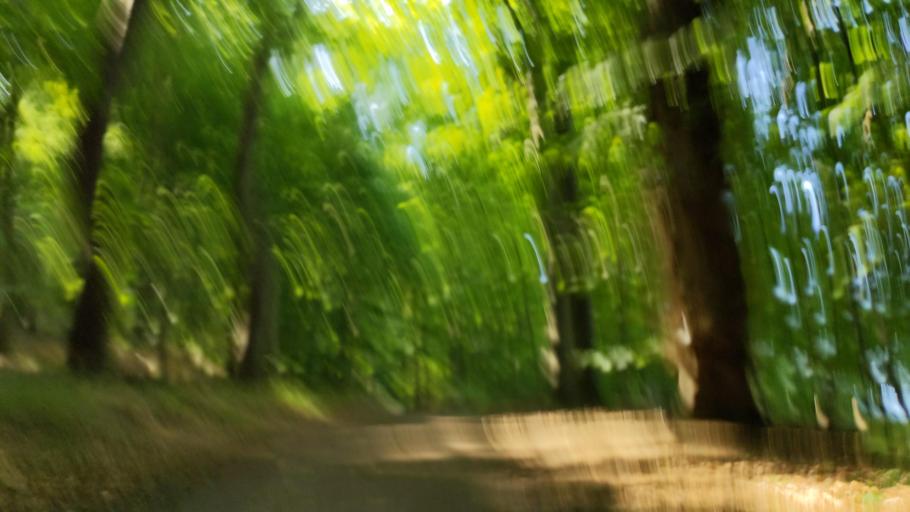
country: DE
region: Schleswig-Holstein
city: Bosdorf
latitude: 54.1618
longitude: 10.5134
